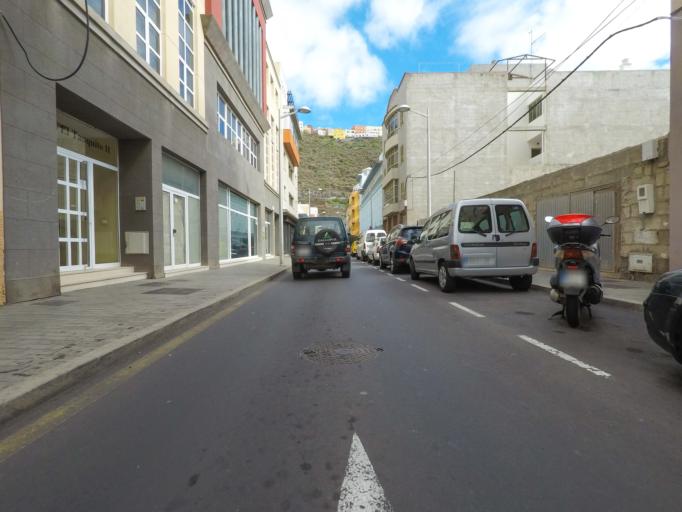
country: ES
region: Canary Islands
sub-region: Provincia de Santa Cruz de Tenerife
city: San Sebastian de la Gomera
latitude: 28.0938
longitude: -17.1140
